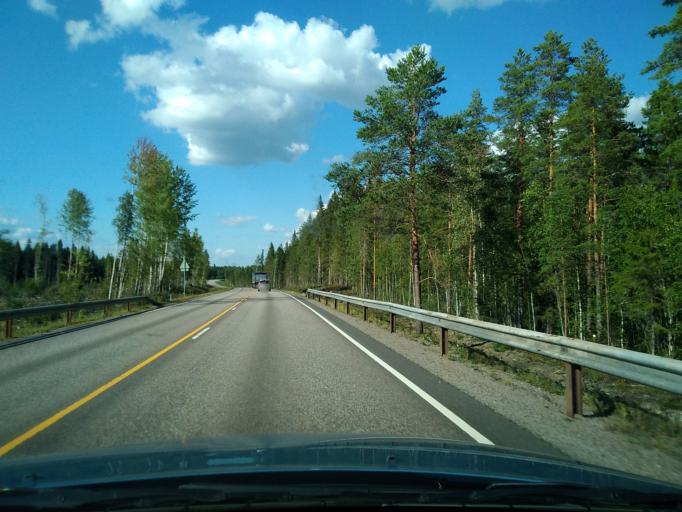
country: FI
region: Central Finland
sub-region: Keuruu
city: Keuruu
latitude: 62.1512
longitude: 24.7501
